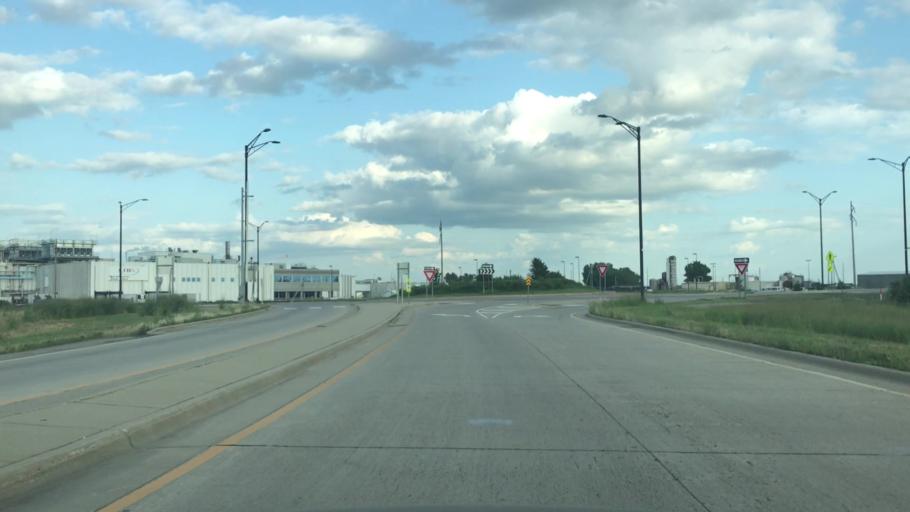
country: US
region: Minnesota
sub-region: Nobles County
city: Worthington
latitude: 43.6362
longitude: -95.5697
